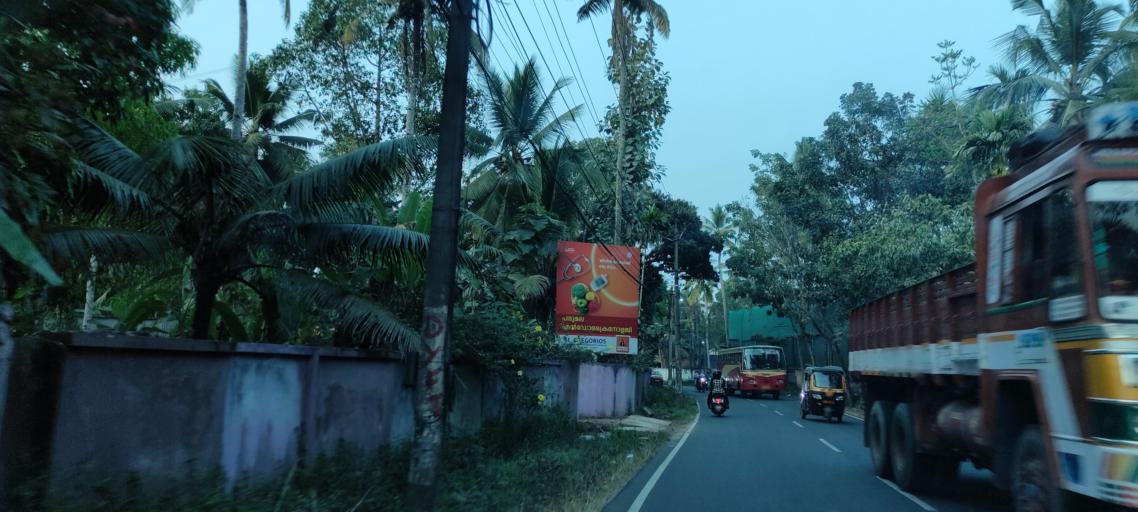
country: IN
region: Kerala
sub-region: Alappuzha
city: Mavelikara
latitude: 9.2698
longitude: 76.5382
